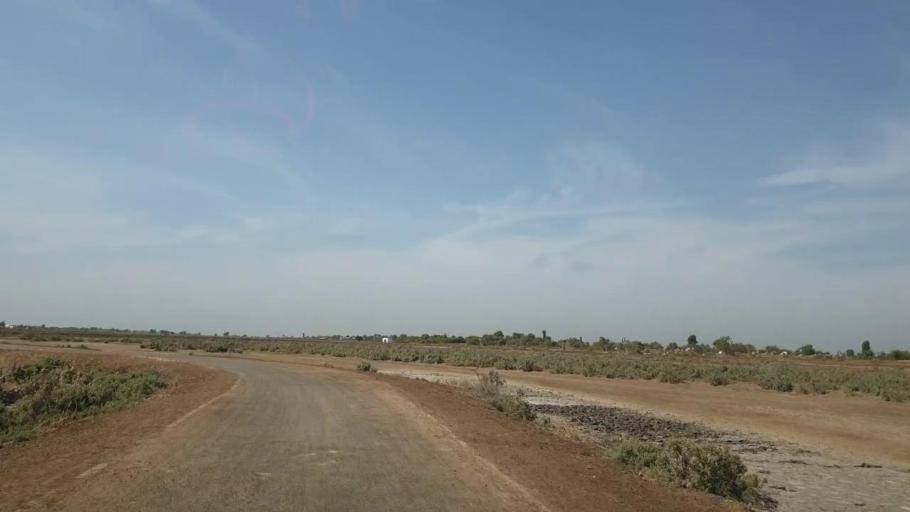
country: PK
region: Sindh
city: Kunri
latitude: 25.2180
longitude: 69.5324
